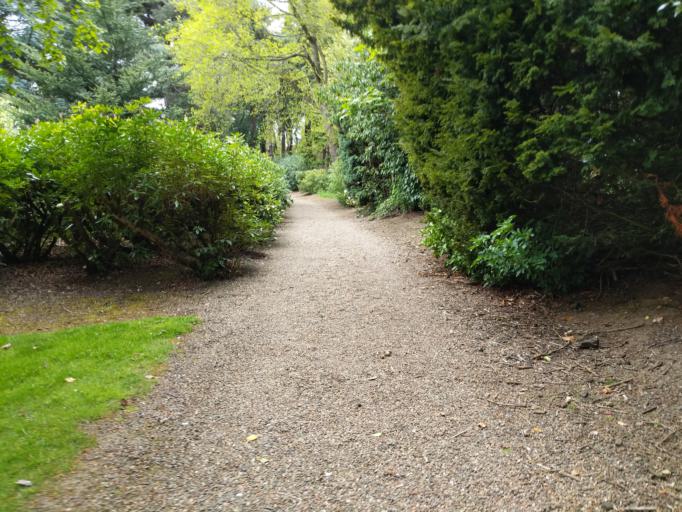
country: GB
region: Scotland
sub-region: Edinburgh
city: Currie
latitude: 55.9098
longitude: -3.3233
